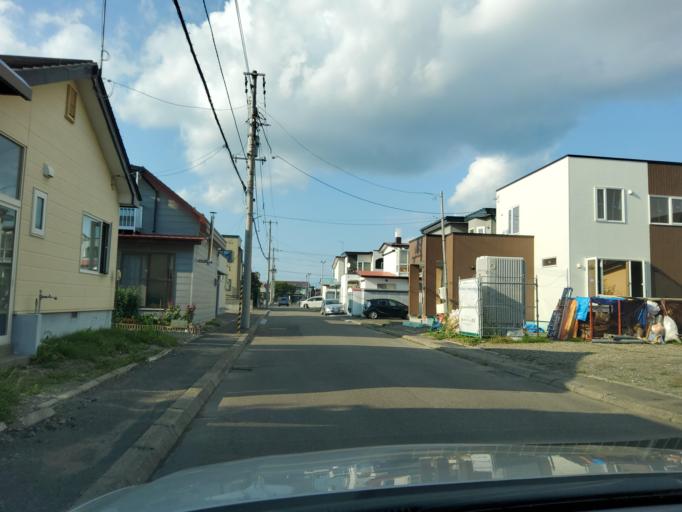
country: JP
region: Hokkaido
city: Obihiro
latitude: 42.9105
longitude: 143.1709
